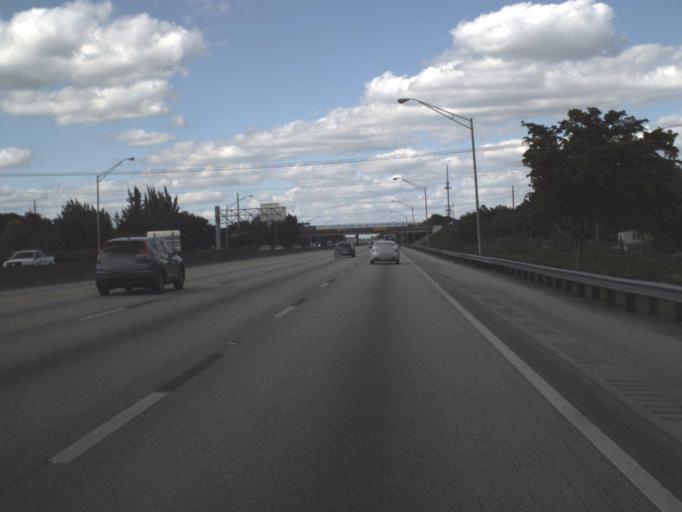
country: US
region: Florida
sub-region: Broward County
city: Pembroke Pines
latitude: 26.0287
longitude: -80.2132
